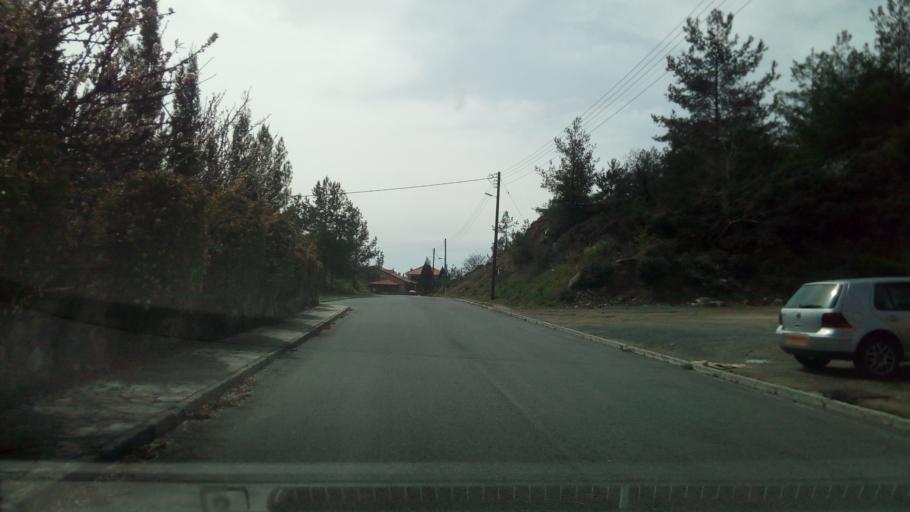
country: CY
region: Limassol
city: Pelendri
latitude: 34.9090
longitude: 33.0108
